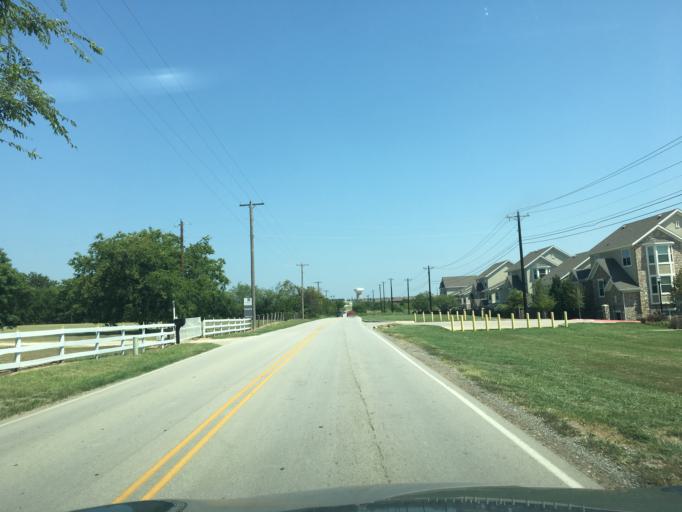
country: US
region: Texas
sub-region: Tarrant County
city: Blue Mound
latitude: 32.9090
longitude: -97.3316
